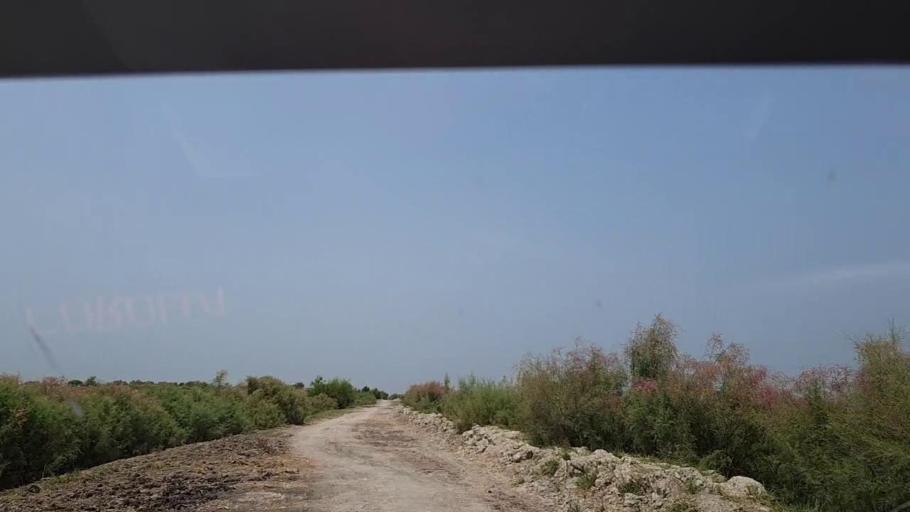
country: PK
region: Sindh
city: Adilpur
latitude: 27.8902
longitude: 69.2516
